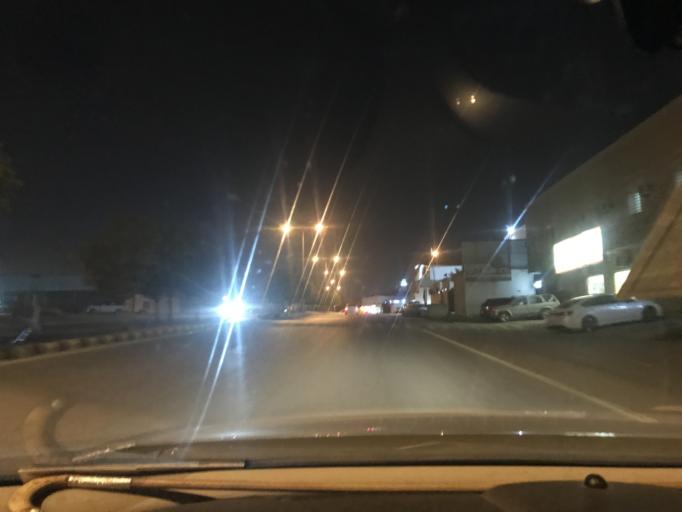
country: SA
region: Ar Riyad
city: Riyadh
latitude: 24.7481
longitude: 46.7536
